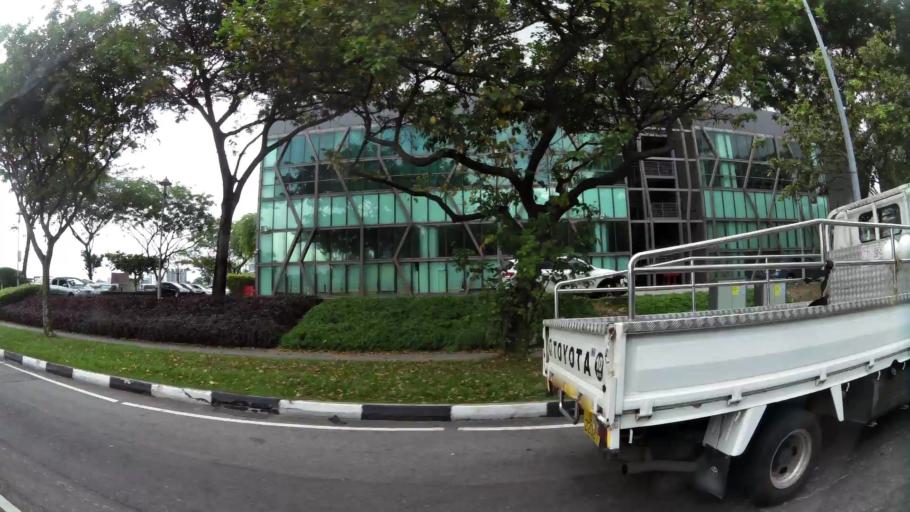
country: MY
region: Johor
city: Johor Bahru
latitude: 1.4617
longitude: 103.8161
